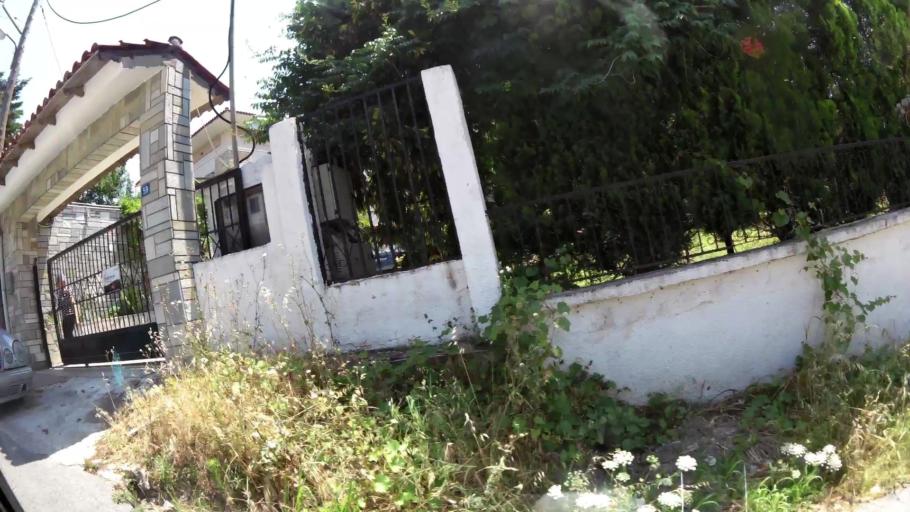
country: GR
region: Central Macedonia
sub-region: Nomos Thessalonikis
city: Plagiari
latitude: 40.4701
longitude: 22.9560
